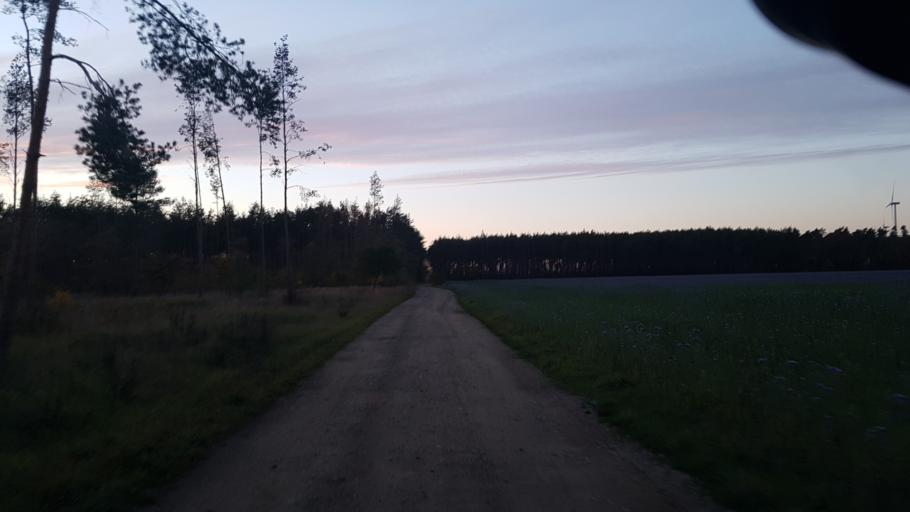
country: DE
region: Brandenburg
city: Bad Liebenwerda
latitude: 51.5062
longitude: 13.3228
